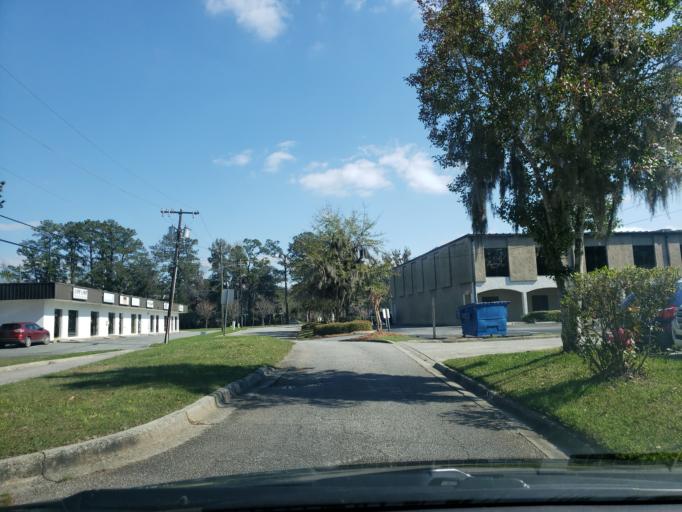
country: US
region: Georgia
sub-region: Chatham County
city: Isle of Hope
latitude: 32.0183
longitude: -81.1131
